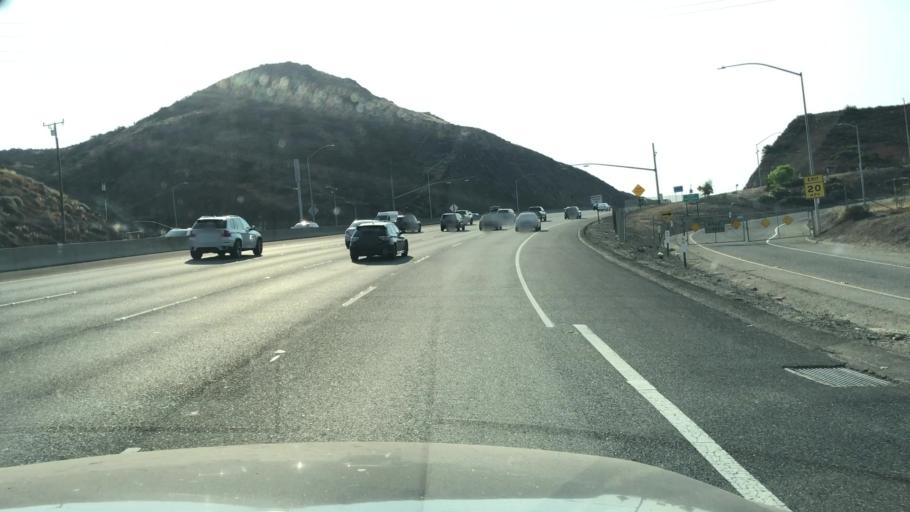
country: US
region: California
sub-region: Ventura County
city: Casa Conejo
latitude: 34.2000
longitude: -118.9586
